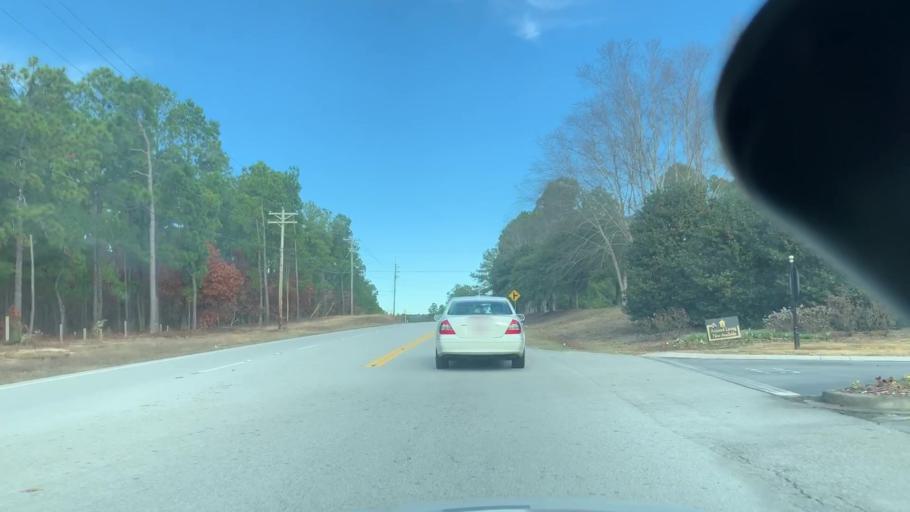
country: US
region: South Carolina
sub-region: Richland County
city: Woodfield
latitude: 34.0879
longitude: -80.8911
